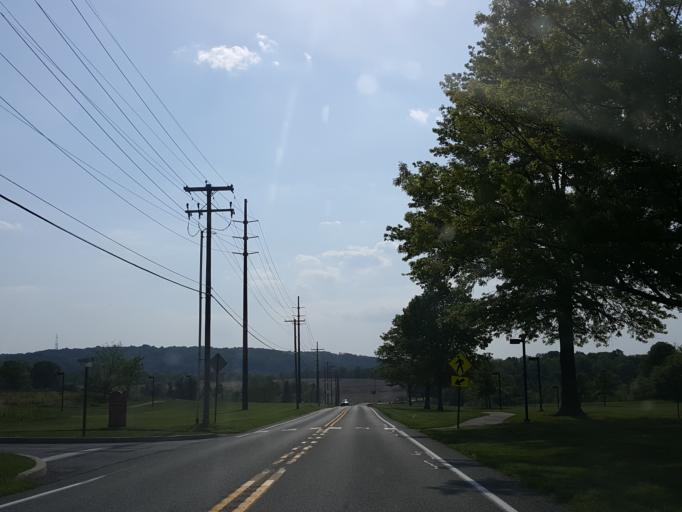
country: US
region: Pennsylvania
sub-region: Dauphin County
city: Hershey
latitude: 40.2611
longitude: -76.6244
